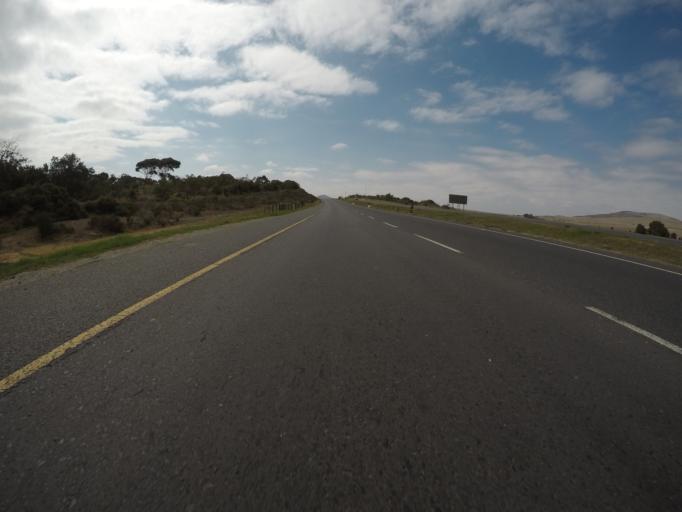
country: ZA
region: Western Cape
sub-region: City of Cape Town
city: Sunset Beach
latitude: -33.7884
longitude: 18.5487
